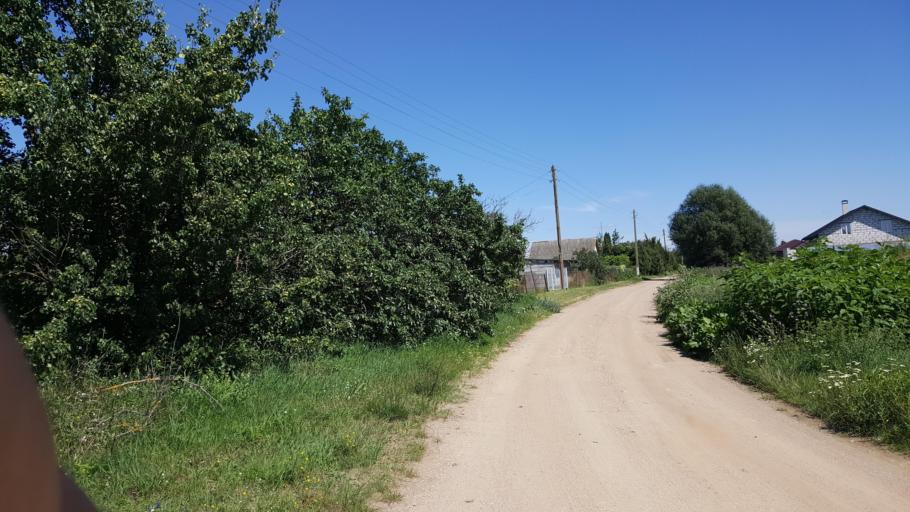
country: BY
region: Brest
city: Charnawchytsy
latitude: 52.2102
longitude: 23.7907
